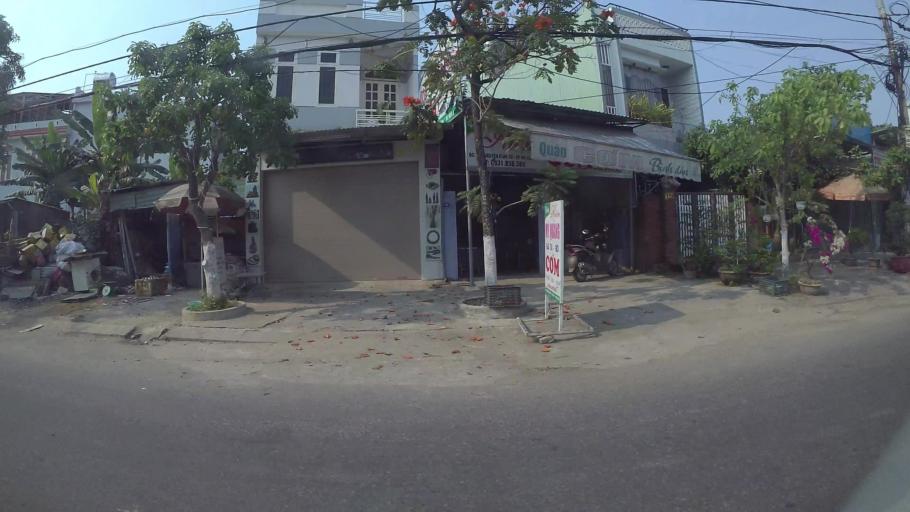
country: VN
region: Da Nang
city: Lien Chieu
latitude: 16.0488
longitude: 108.1719
